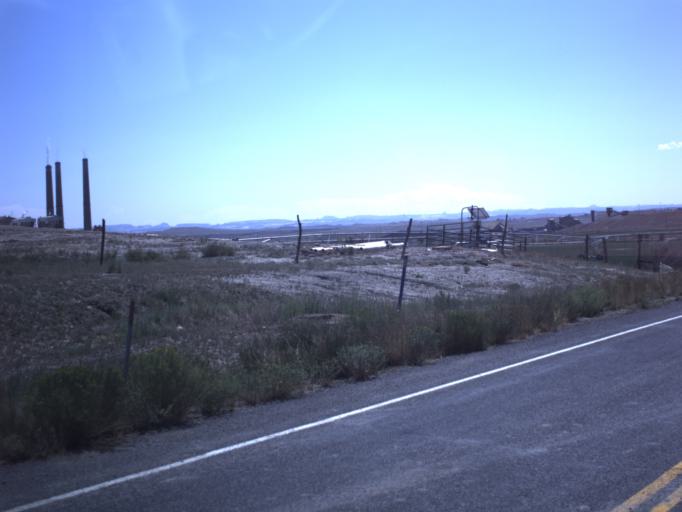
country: US
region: Utah
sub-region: Emery County
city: Castle Dale
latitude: 39.1836
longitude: -111.0477
